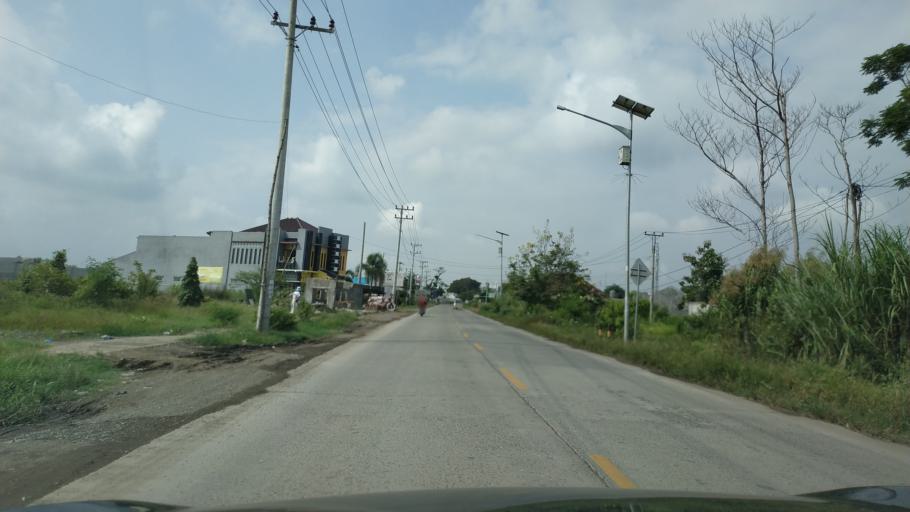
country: ID
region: Central Java
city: Ketanggungan
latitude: -6.8997
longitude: 108.8877
